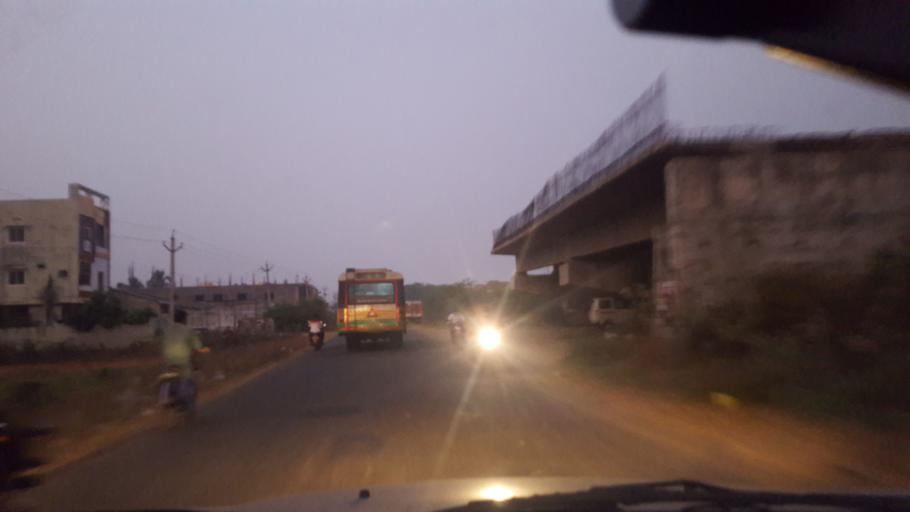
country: IN
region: Andhra Pradesh
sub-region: Srikakulam
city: Palasa
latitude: 18.7525
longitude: 84.4165
